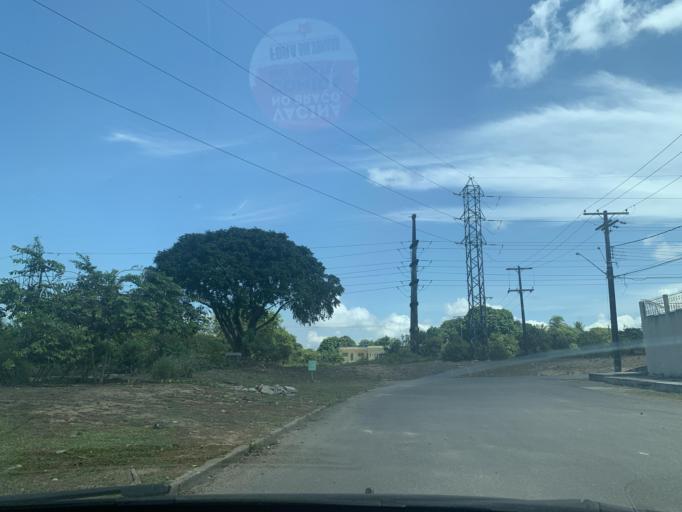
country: BR
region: Amazonas
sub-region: Manaus
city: Manaus
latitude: -3.1125
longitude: -59.9708
